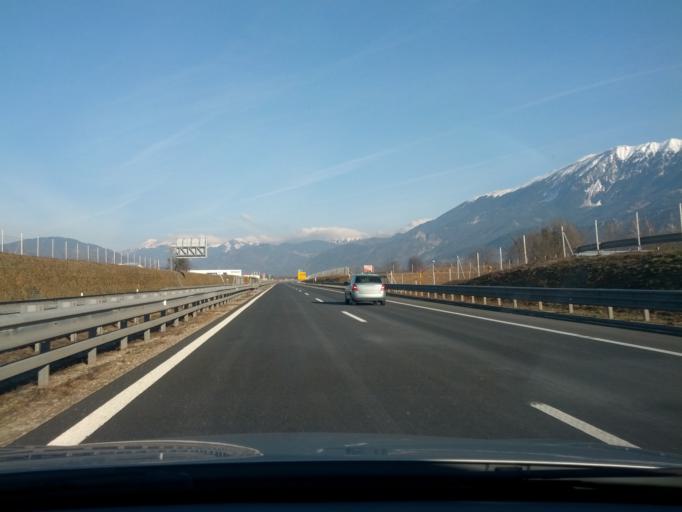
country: SI
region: Radovljica
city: Lesce
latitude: 46.3618
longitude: 14.1667
